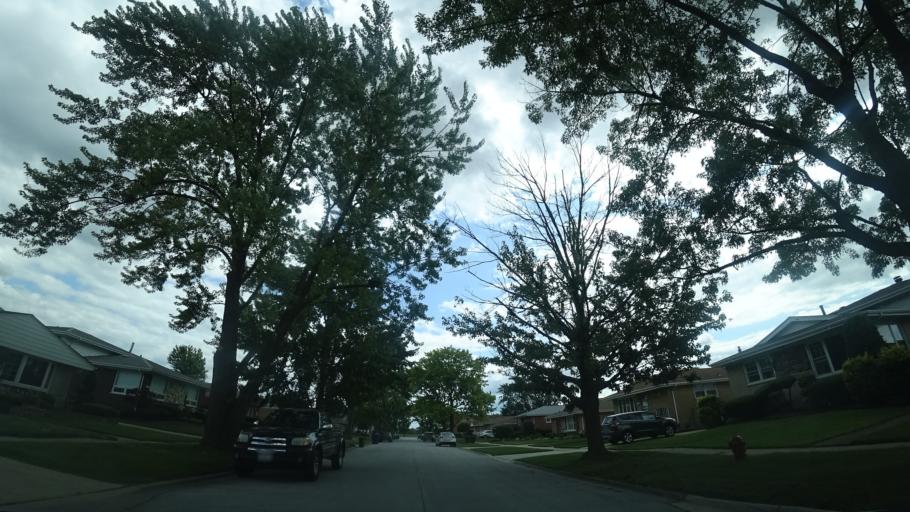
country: US
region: Illinois
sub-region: Cook County
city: Alsip
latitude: 41.6929
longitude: -87.7313
